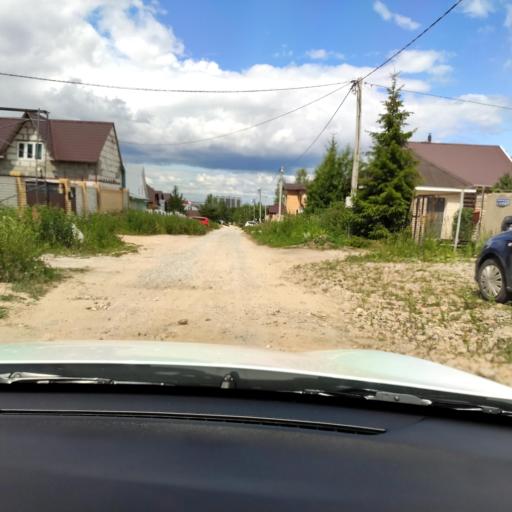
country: RU
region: Tatarstan
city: Vysokaya Gora
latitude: 55.7825
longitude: 49.2723
